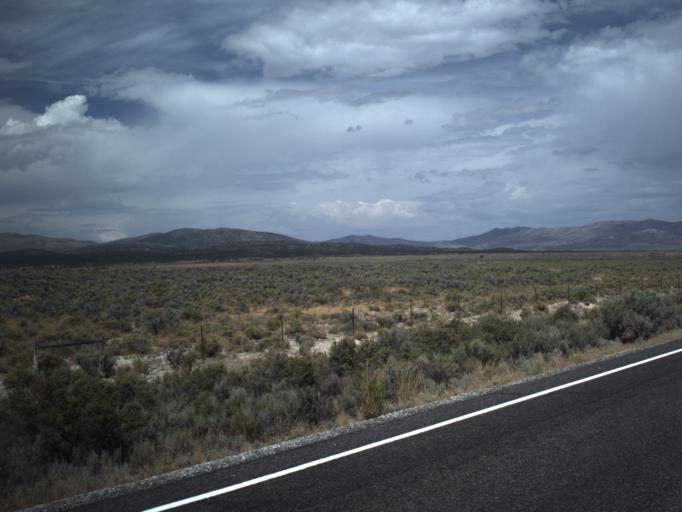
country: US
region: Idaho
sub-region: Cassia County
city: Burley
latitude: 41.6885
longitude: -113.5379
